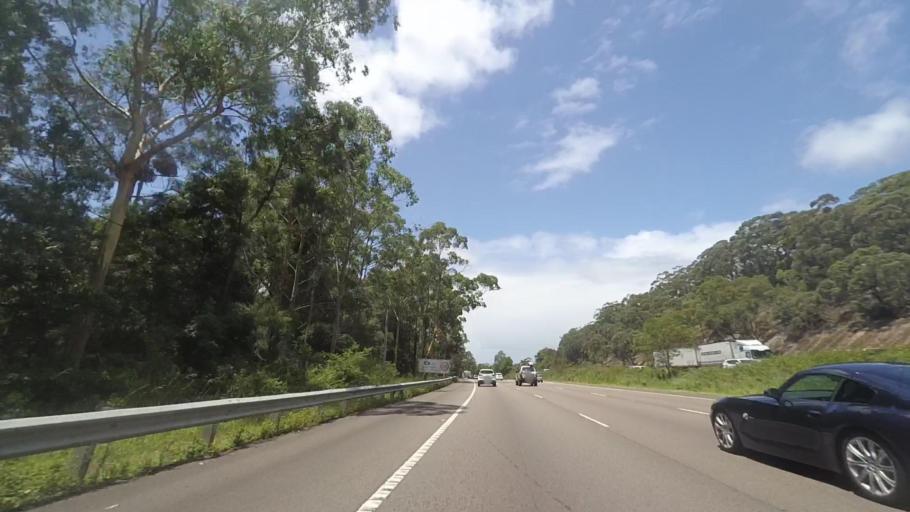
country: AU
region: New South Wales
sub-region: Gosford Shire
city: Lisarow
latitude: -33.3587
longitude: 151.3417
